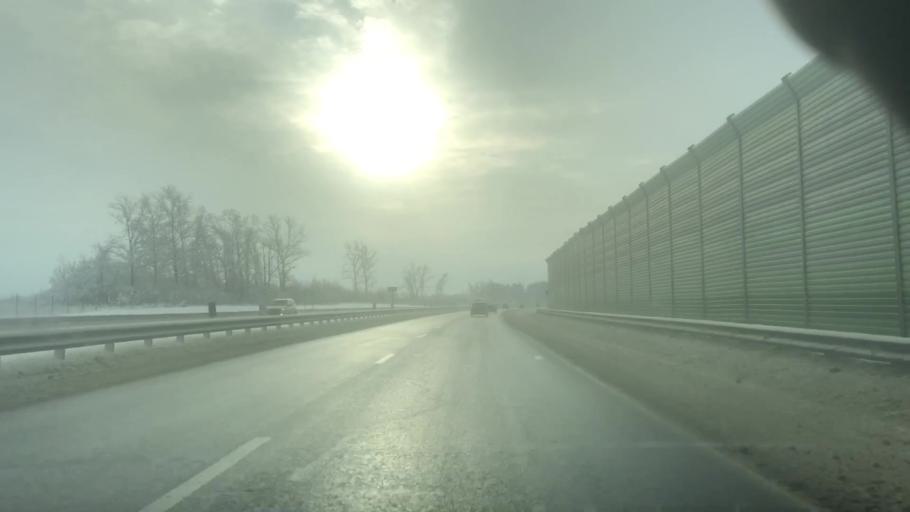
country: RU
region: Tula
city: Venev
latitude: 54.2749
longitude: 38.1604
